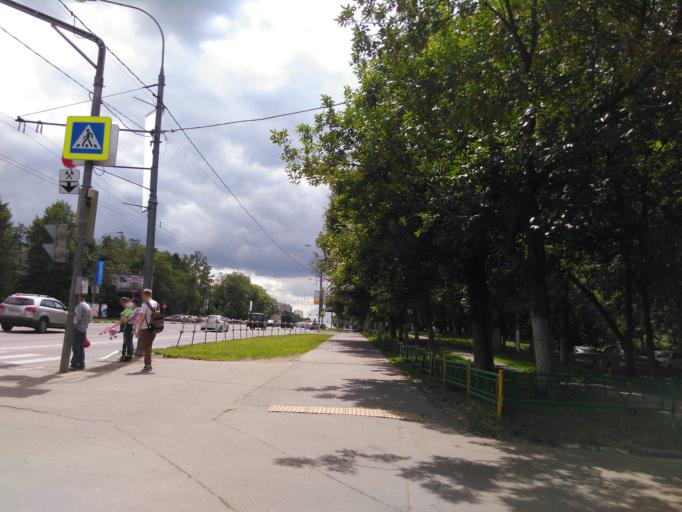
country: RU
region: Moscow
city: Zyuzino
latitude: 55.6594
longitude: 37.5739
